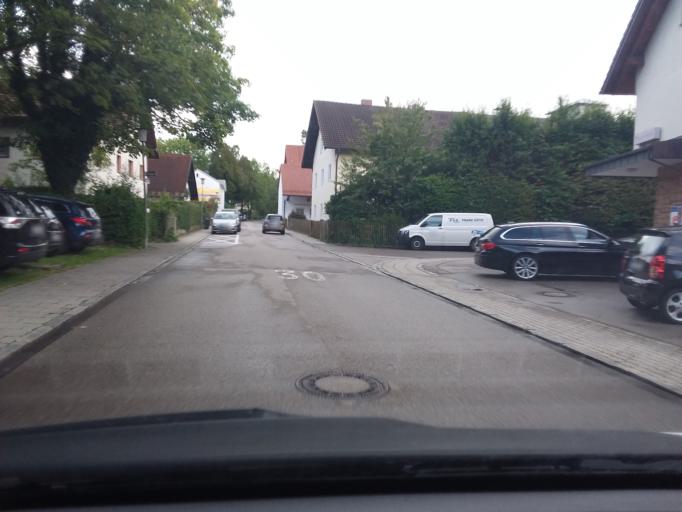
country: DE
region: Bavaria
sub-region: Upper Bavaria
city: Ismaning
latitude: 48.2312
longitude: 11.6737
